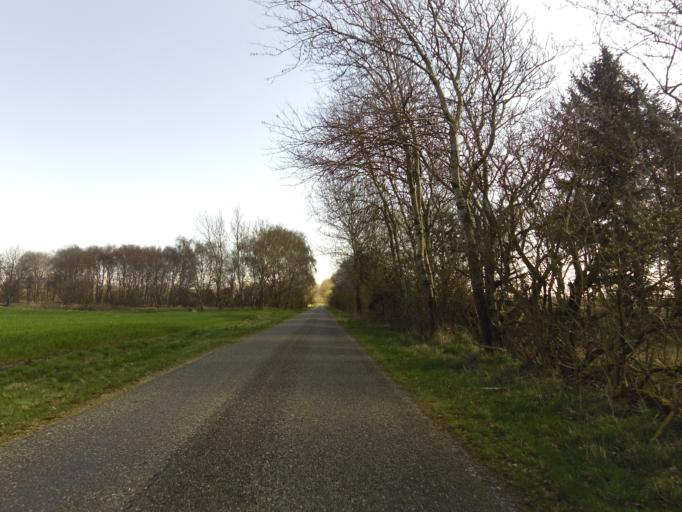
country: DK
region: South Denmark
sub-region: Esbjerg Kommune
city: Ribe
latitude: 55.3443
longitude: 8.8507
